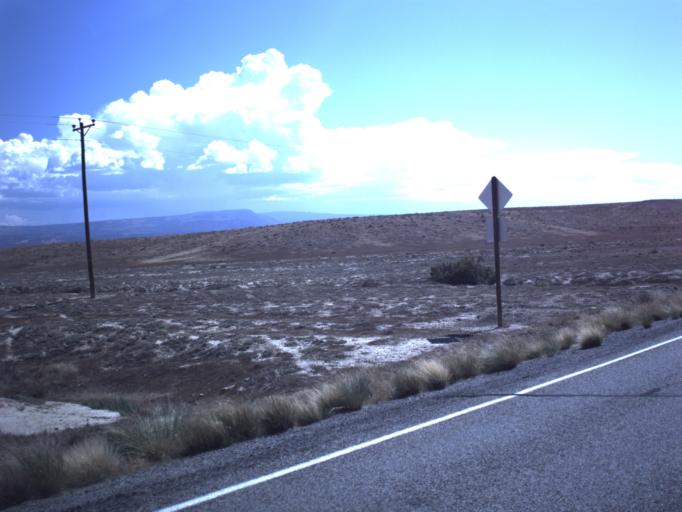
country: US
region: Utah
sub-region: Grand County
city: Moab
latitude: 38.9403
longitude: -109.3495
